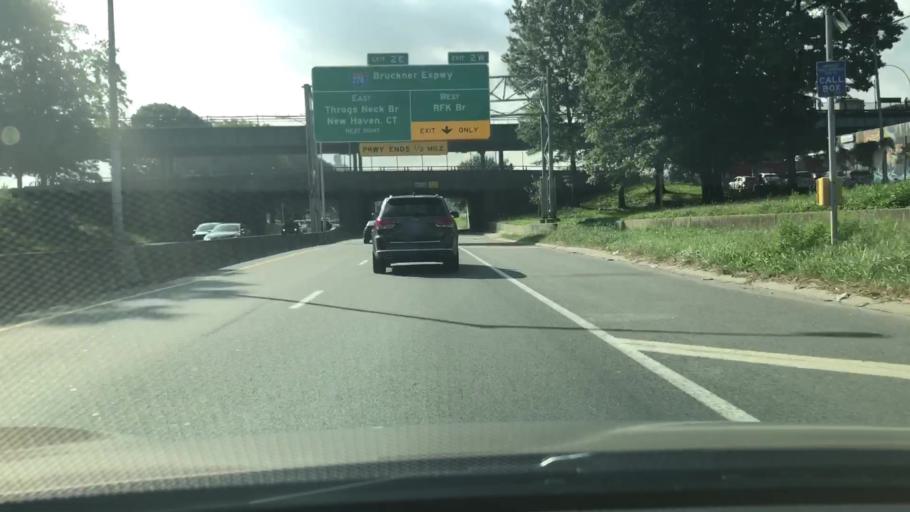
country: US
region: New York
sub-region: Bronx
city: The Bronx
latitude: 40.8306
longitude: -73.8738
